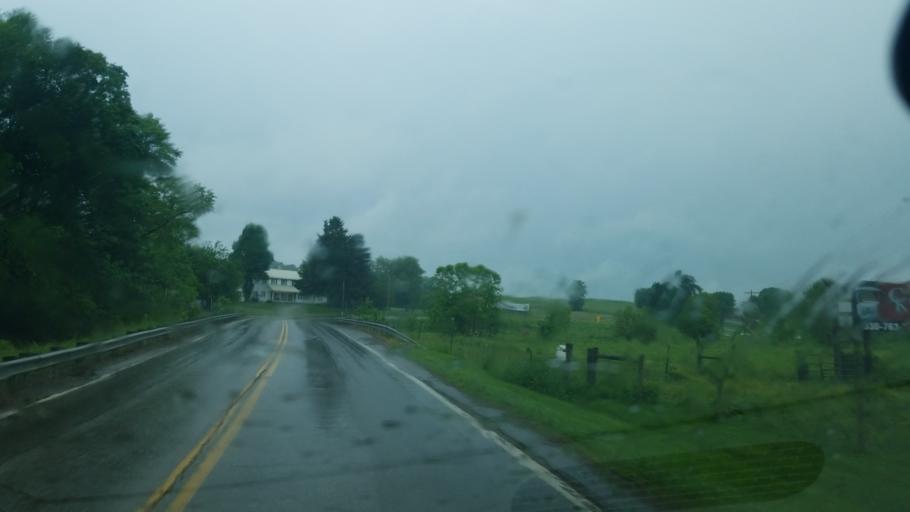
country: US
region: Ohio
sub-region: Holmes County
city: Millersburg
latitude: 40.5318
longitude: -81.8106
